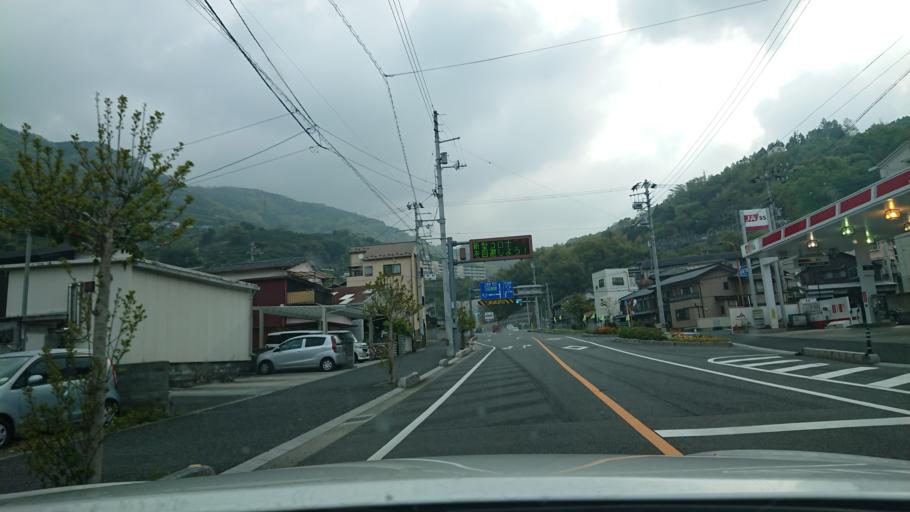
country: JP
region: Ehime
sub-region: Nishiuwa-gun
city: Ikata-cho
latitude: 33.4668
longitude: 132.4273
